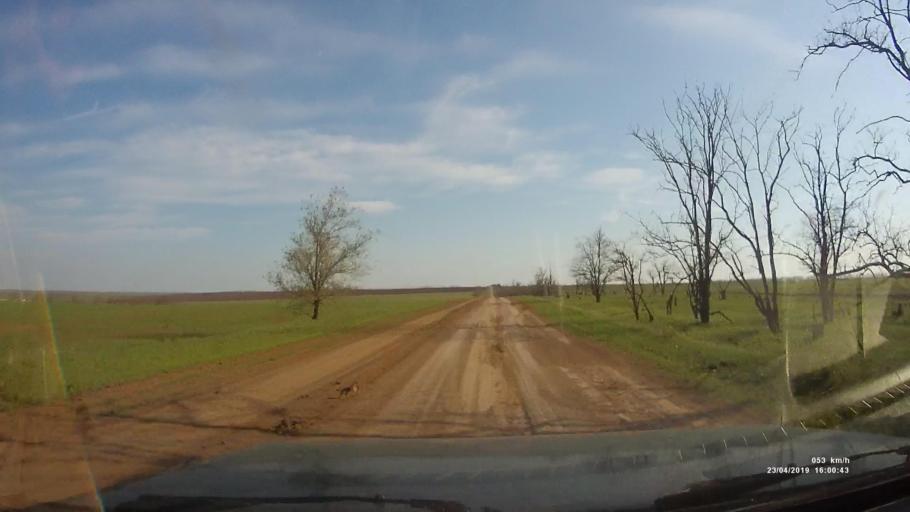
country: RU
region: Rostov
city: Remontnoye
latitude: 46.5072
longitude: 43.1070
